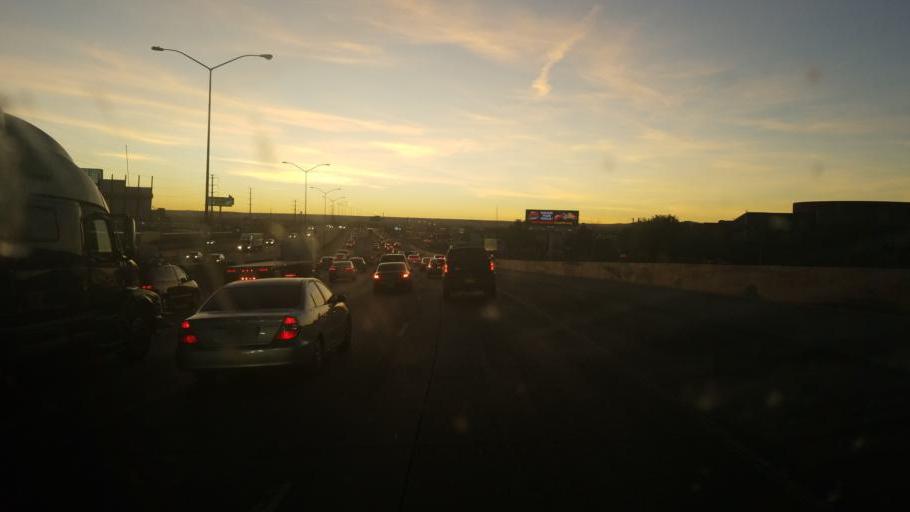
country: US
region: New Mexico
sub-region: Bernalillo County
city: Albuquerque
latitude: 35.1073
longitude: -106.6525
